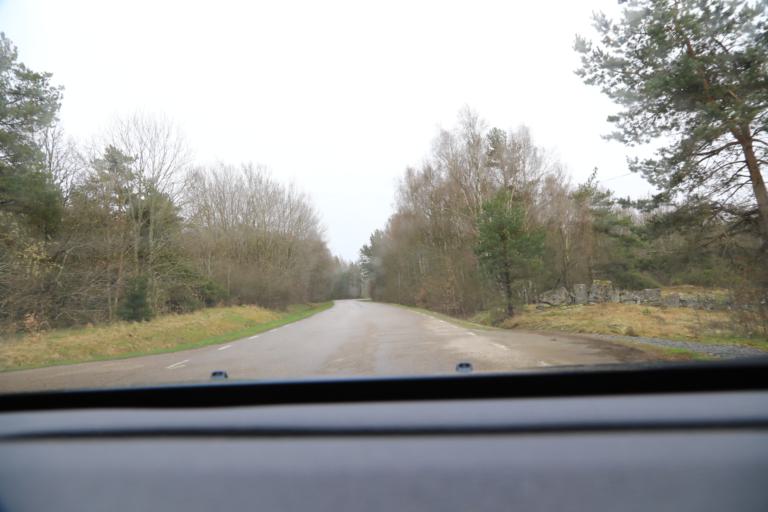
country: SE
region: Halland
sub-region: Kungsbacka Kommun
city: Frillesas
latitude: 57.2903
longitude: 12.2142
